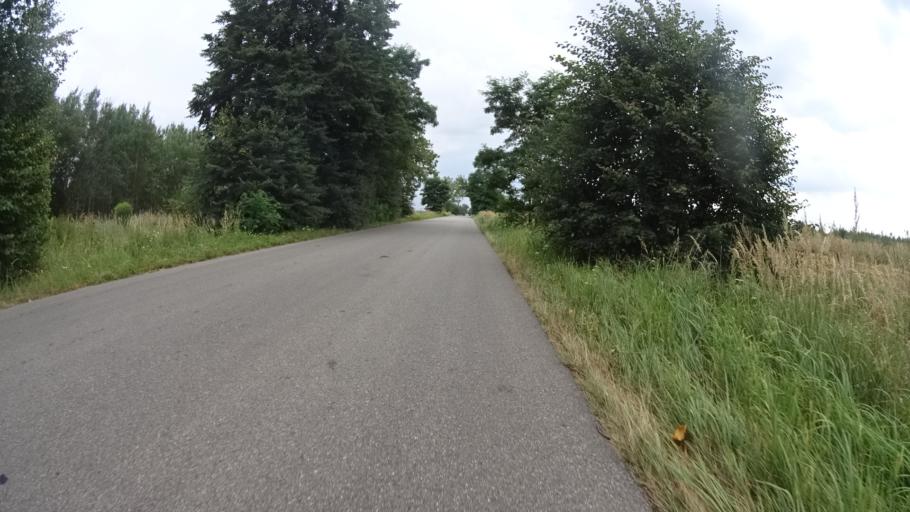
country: PL
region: Masovian Voivodeship
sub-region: Powiat grojecki
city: Goszczyn
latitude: 51.6762
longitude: 20.8588
